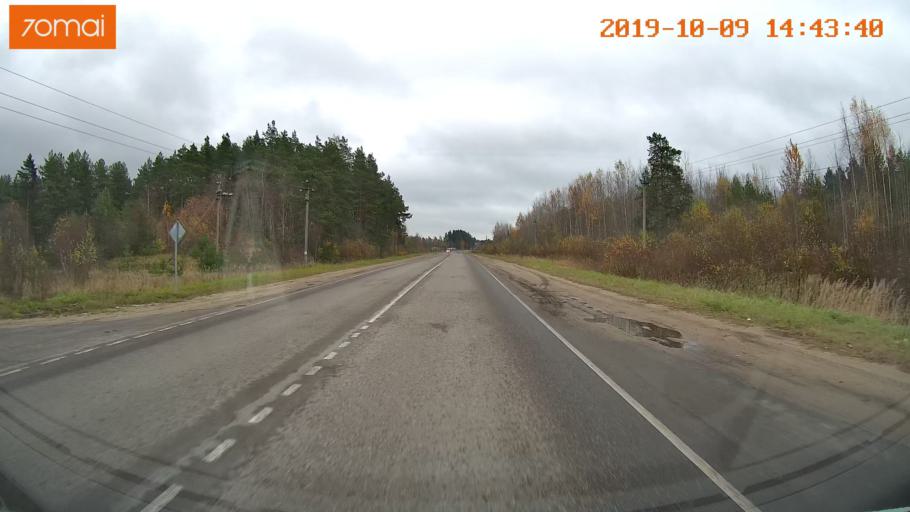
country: RU
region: Kostroma
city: Buy
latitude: 58.4568
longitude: 41.5488
